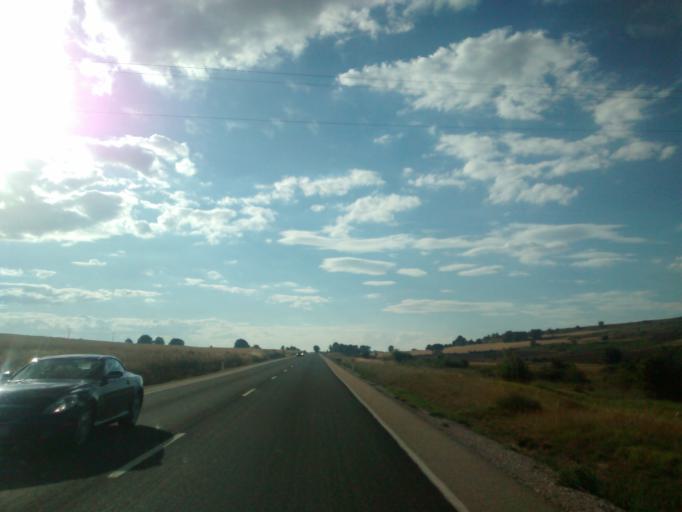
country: ES
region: Castille and Leon
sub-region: Provincia de Burgos
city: Basconcillos del Tozo
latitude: 42.6669
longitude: -3.9229
